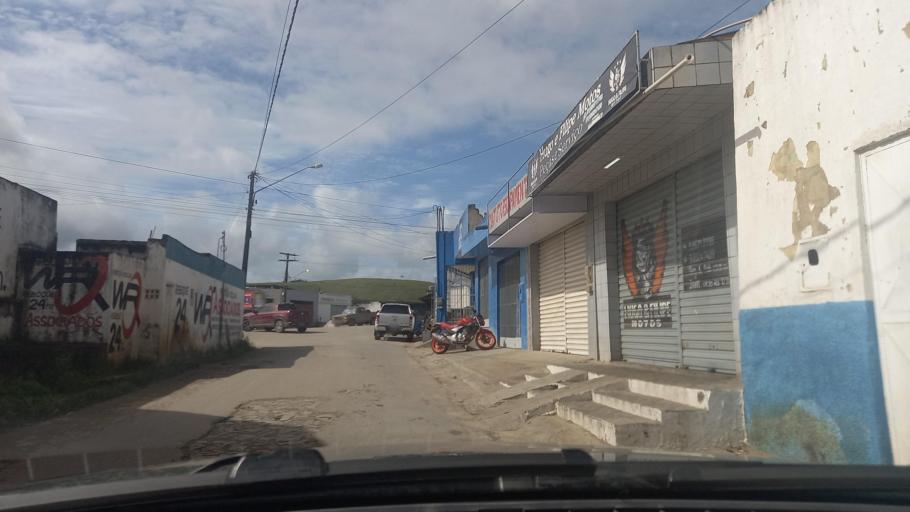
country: BR
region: Pernambuco
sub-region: Vitoria De Santo Antao
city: Vitoria de Santo Antao
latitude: -8.1247
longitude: -35.2828
